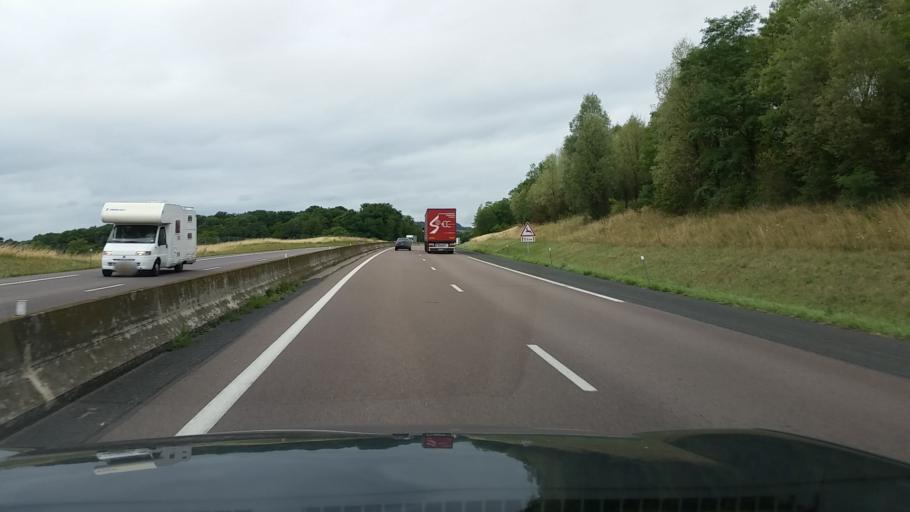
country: FR
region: Lorraine
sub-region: Departement des Vosges
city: Chatenois
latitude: 48.3391
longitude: 5.8535
